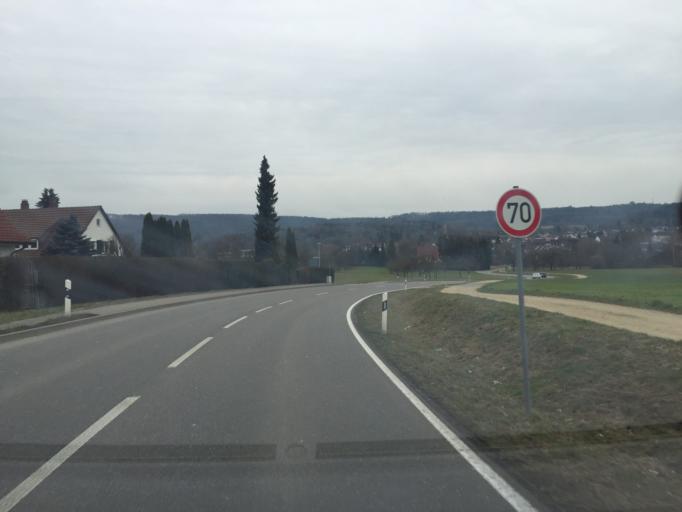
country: DE
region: Baden-Wuerttemberg
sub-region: Freiburg Region
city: Gottmadingen
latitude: 47.7287
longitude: 8.7561
